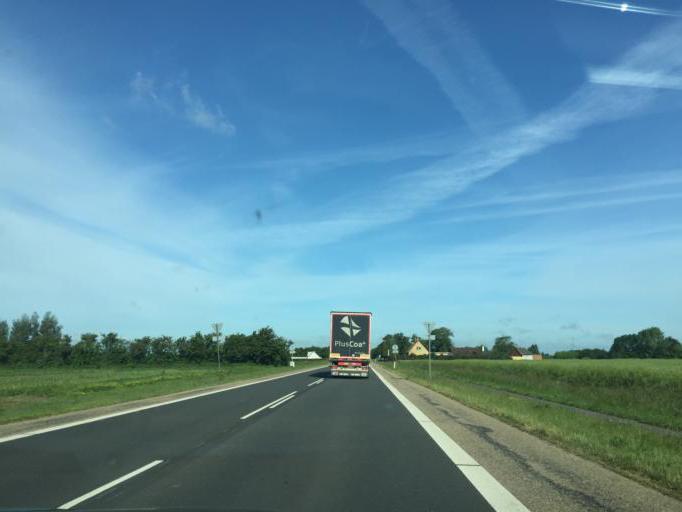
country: DK
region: South Denmark
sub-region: Middelfart Kommune
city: Norre Aby
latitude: 55.4703
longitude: 9.8907
